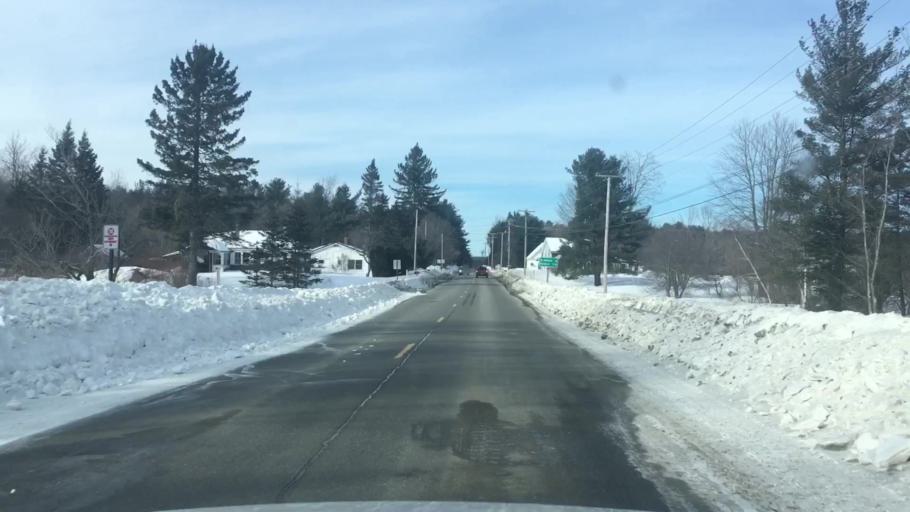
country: US
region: Maine
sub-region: Penobscot County
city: Charleston
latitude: 45.0511
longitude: -69.0300
